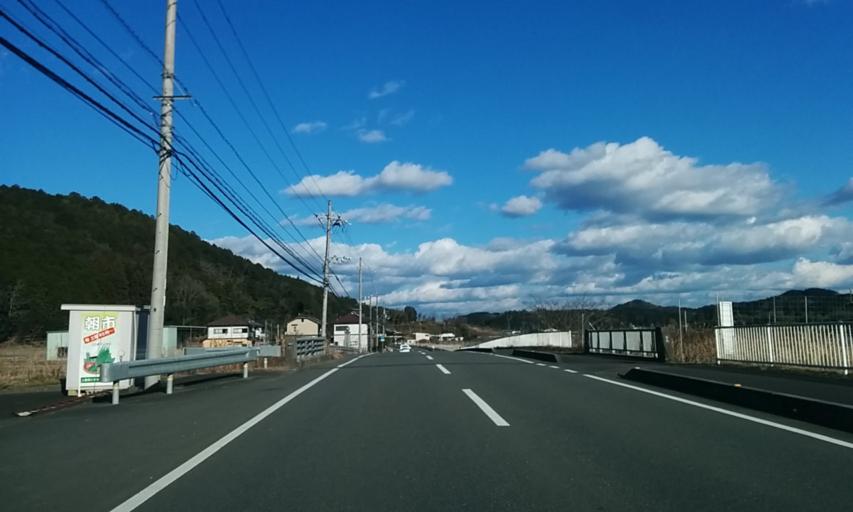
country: JP
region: Kyoto
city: Fukuchiyama
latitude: 35.2843
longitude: 135.0536
